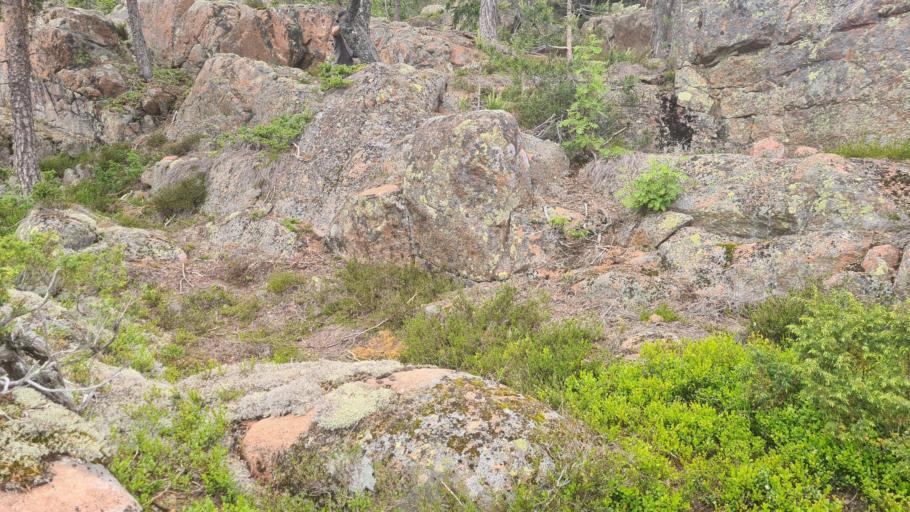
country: SE
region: Vaesternorrland
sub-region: Kramfors Kommun
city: Nordingra
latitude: 62.9833
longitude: 18.4010
